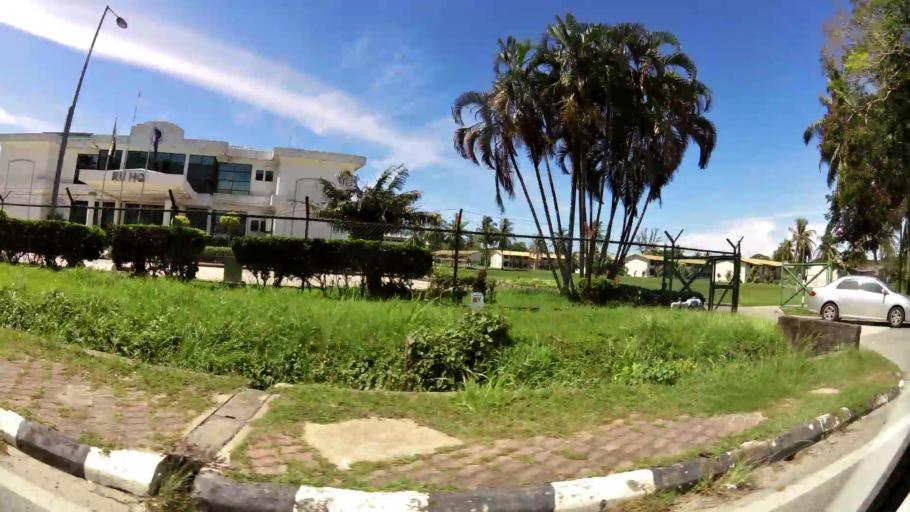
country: BN
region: Brunei and Muara
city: Bandar Seri Begawan
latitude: 5.0293
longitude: 115.0636
